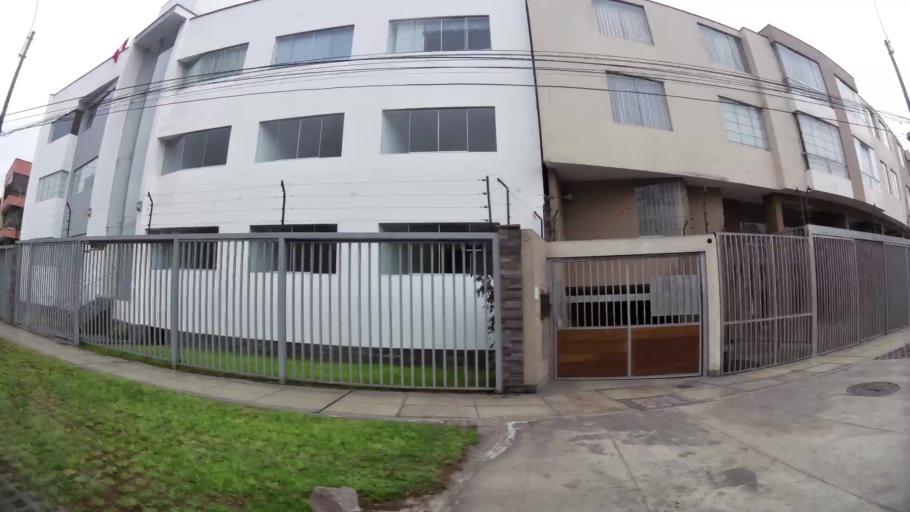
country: PE
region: Lima
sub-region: Lima
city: La Molina
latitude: -12.0732
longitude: -76.9399
